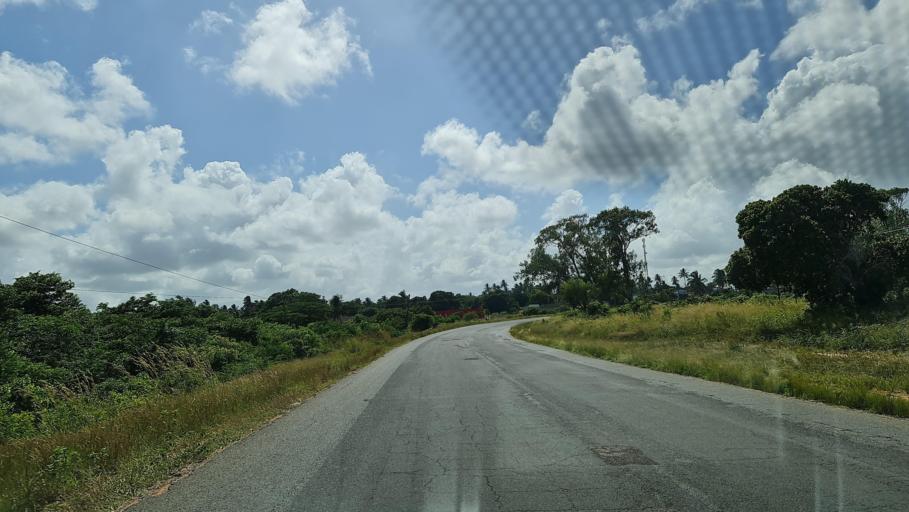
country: MZ
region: Gaza
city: Manjacaze
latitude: -24.6738
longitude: 34.5730
